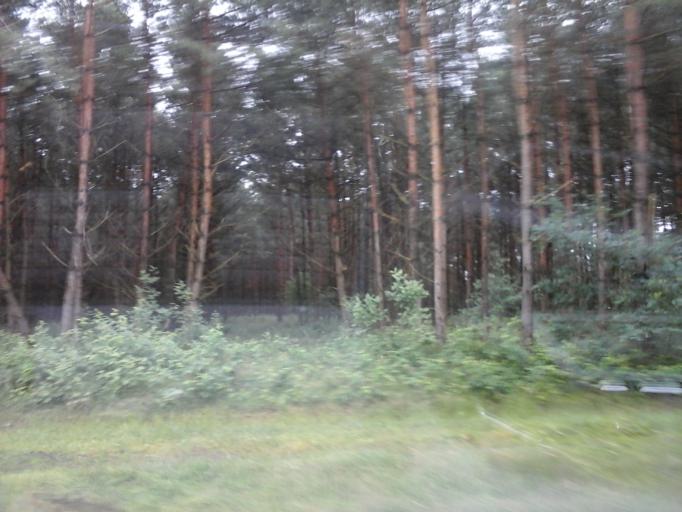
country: PL
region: West Pomeranian Voivodeship
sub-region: Powiat choszczenski
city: Krzecin
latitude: 52.9910
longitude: 15.5593
